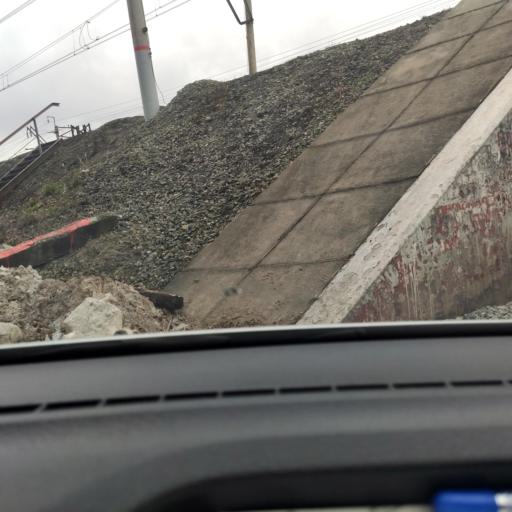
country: RU
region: Bashkortostan
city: Avdon
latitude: 54.6225
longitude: 55.5995
